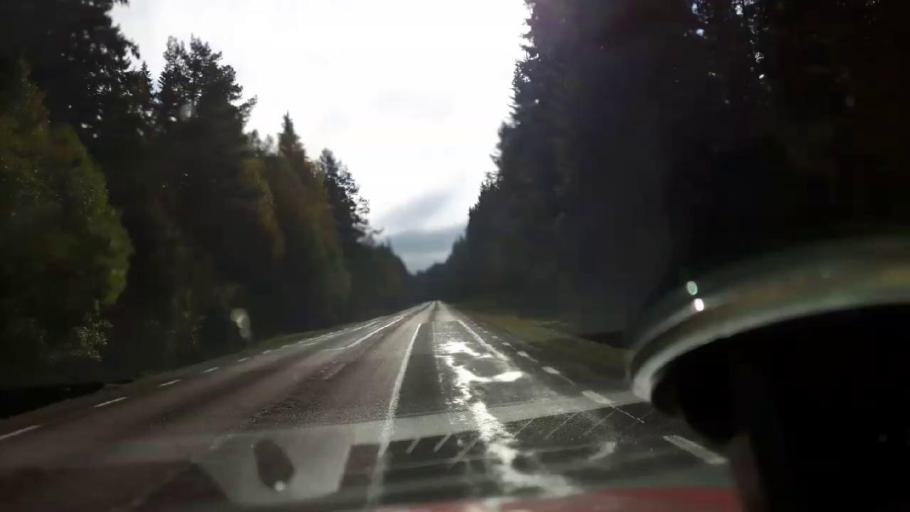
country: SE
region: Gaevleborg
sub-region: Ljusdals Kommun
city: Farila
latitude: 61.8837
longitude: 15.7065
